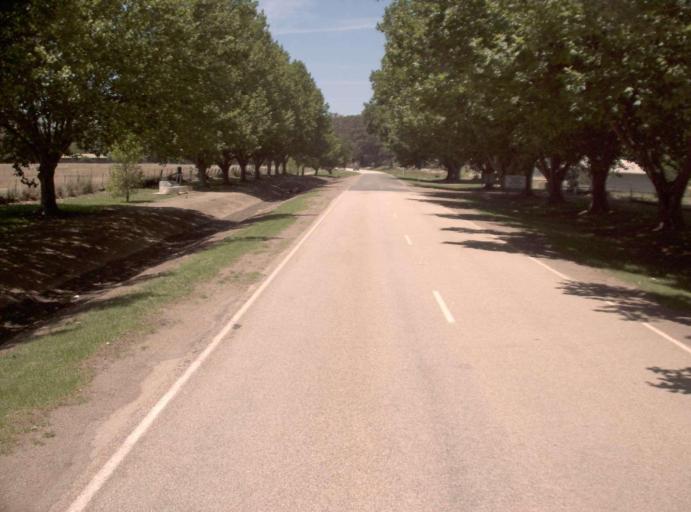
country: AU
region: Victoria
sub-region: East Gippsland
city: Bairnsdale
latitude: -37.2697
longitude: 147.7252
